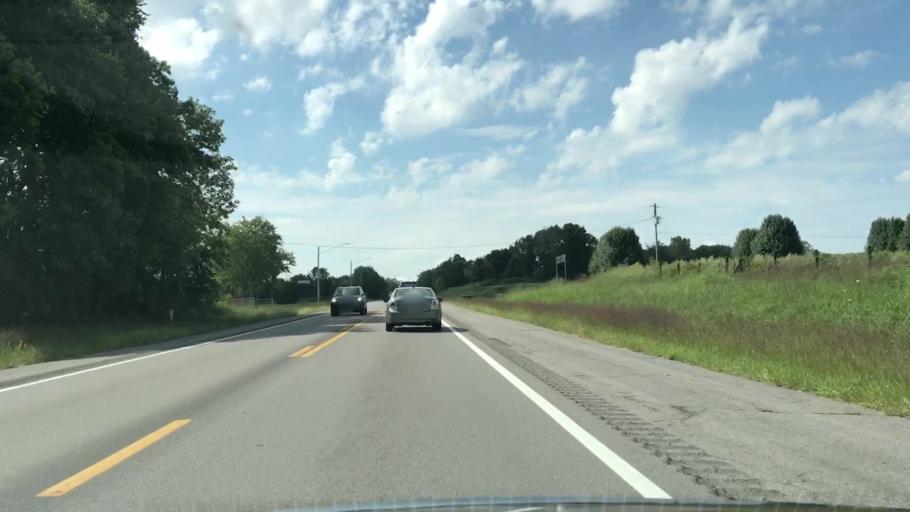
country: US
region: Tennessee
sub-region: Sumner County
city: Westmoreland
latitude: 36.5830
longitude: -86.2391
